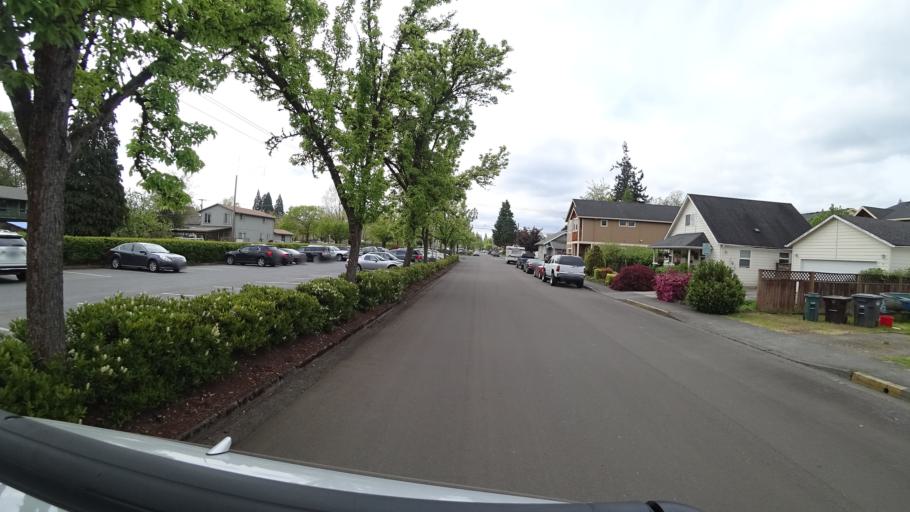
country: US
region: Oregon
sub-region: Washington County
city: Hillsboro
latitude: 45.5260
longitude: -122.9915
